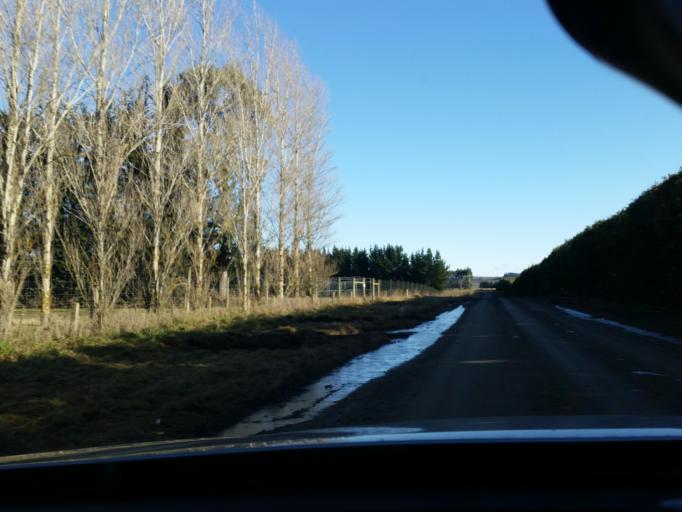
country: NZ
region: Southland
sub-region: Gore District
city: Gore
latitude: -45.7911
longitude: 168.6692
